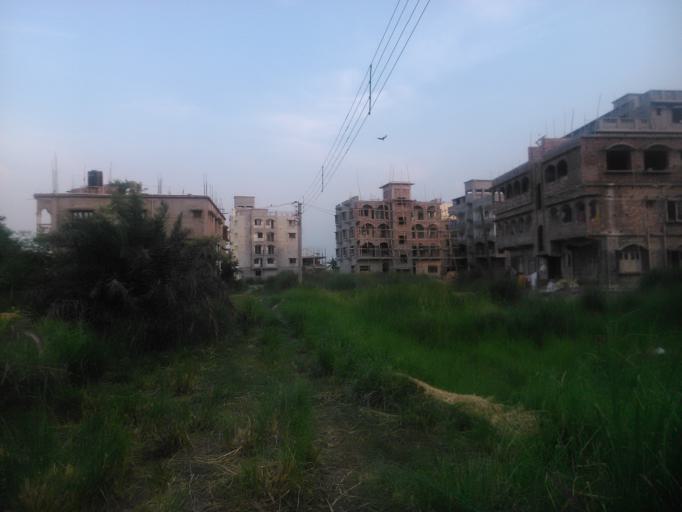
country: IN
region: West Bengal
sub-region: Nadia
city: Navadwip
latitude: 23.4325
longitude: 88.3910
